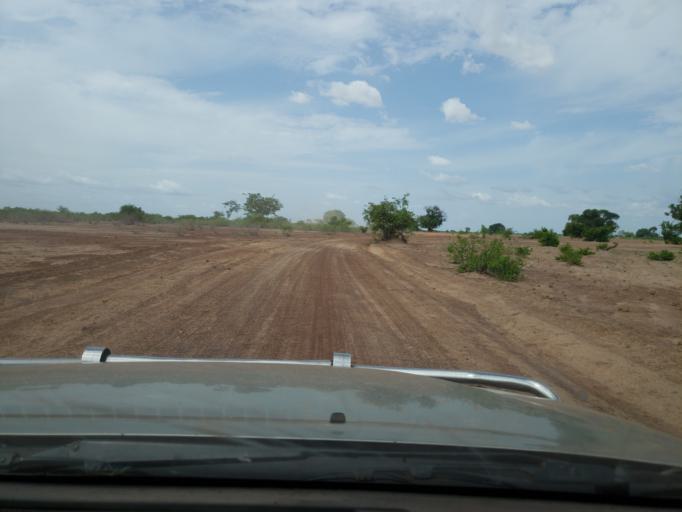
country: ML
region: Segou
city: Bla
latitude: 12.7410
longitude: -5.6510
